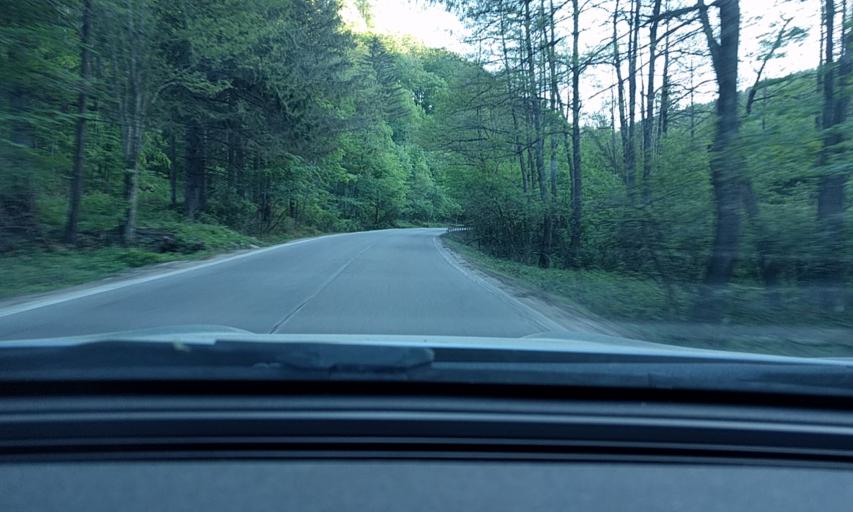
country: RO
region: Bacau
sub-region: Oras Slanic-Moldova
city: Slanic-Moldova
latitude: 46.1115
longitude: 26.4168
